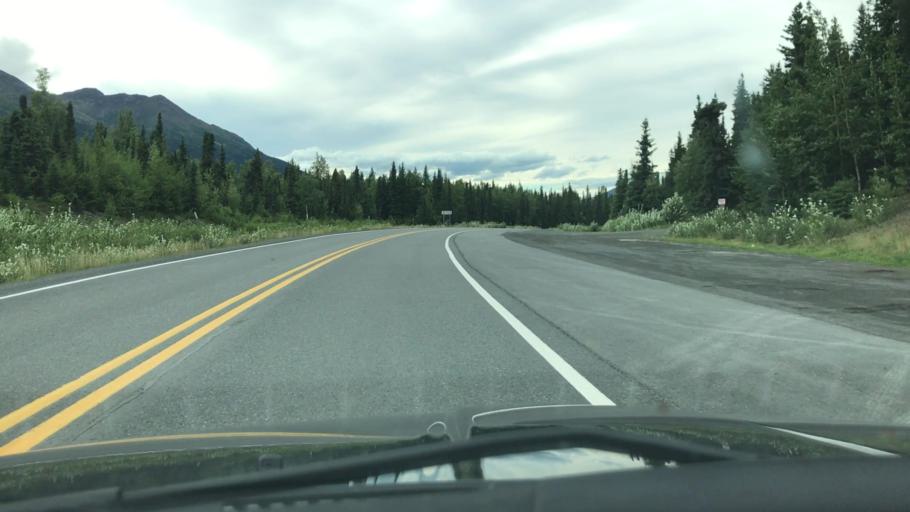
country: US
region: Alaska
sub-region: Kenai Peninsula Borough
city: Seward
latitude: 60.4836
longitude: -149.9529
